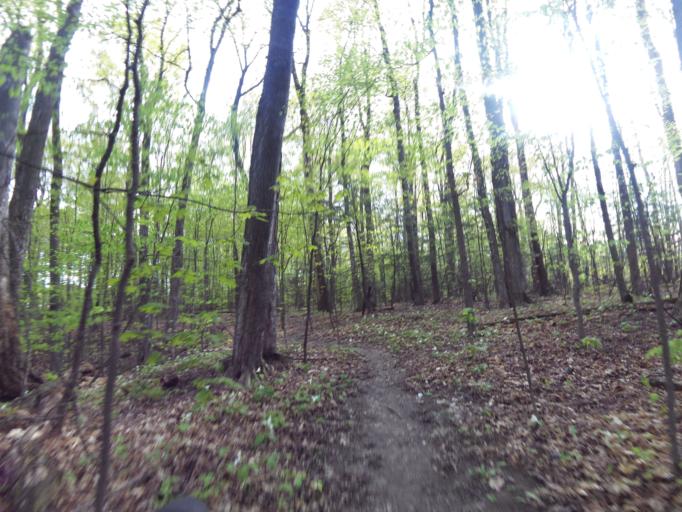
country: CA
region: Ontario
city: Bells Corners
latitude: 45.2914
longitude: -75.7173
